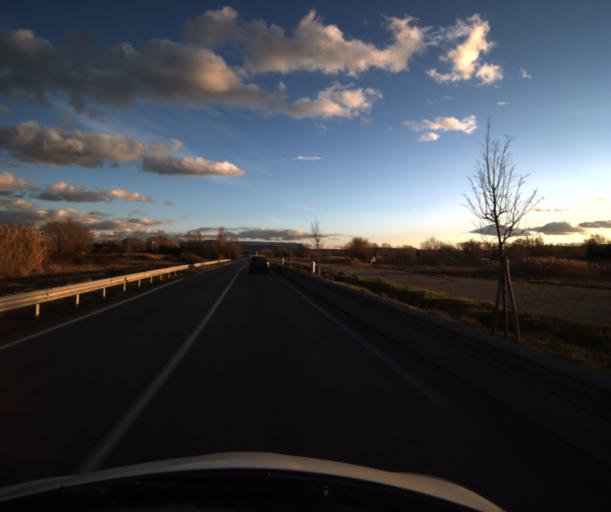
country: FR
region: Provence-Alpes-Cote d'Azur
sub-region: Departement du Vaucluse
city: Pertuis
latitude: 43.6772
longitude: 5.4908
